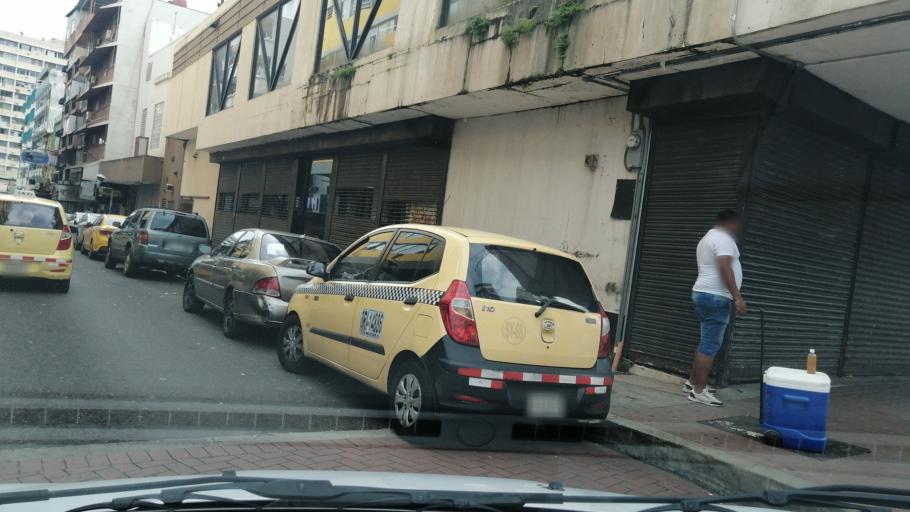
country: PA
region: Panama
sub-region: Distrito de Panama
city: Ancon
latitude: 8.9586
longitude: -79.5411
